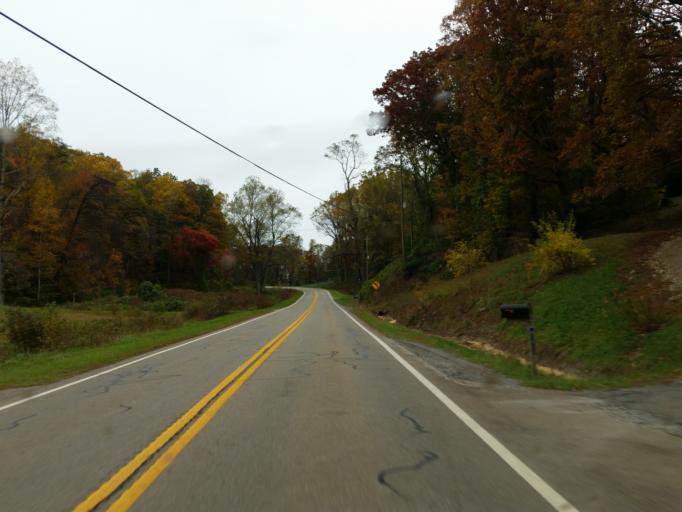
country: US
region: Georgia
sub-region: Pickens County
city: Jasper
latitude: 34.5303
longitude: -84.4024
